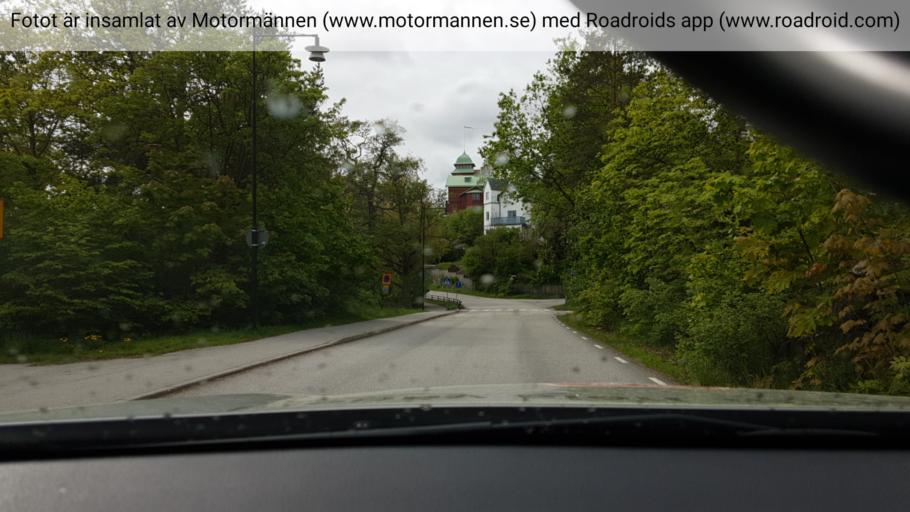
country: SE
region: Stockholm
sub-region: Nacka Kommun
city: Saltsjobaden
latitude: 59.2777
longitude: 18.3106
